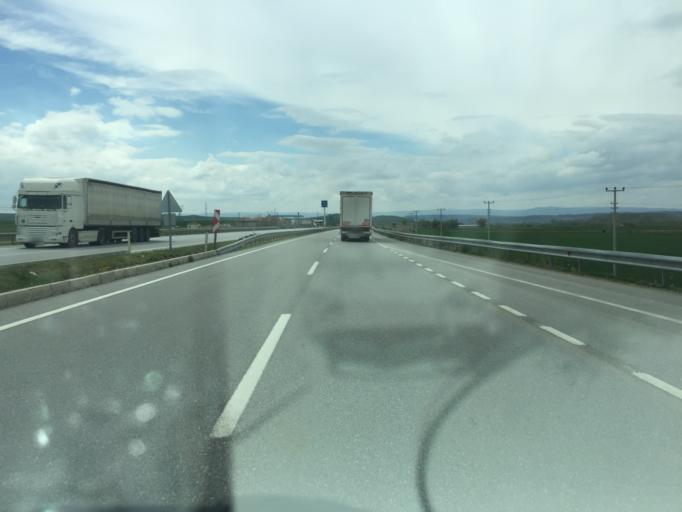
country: TR
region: Corum
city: Sungurlu
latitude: 40.1436
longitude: 34.2825
